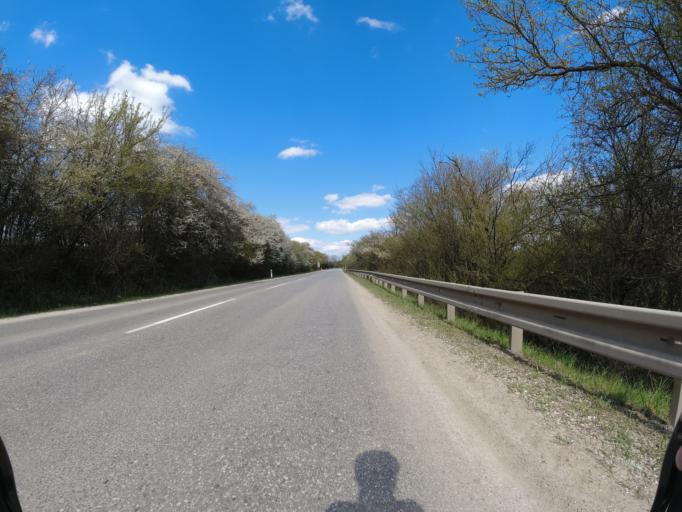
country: SK
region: Nitriansky
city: Stara Tura
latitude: 48.7797
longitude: 17.7078
